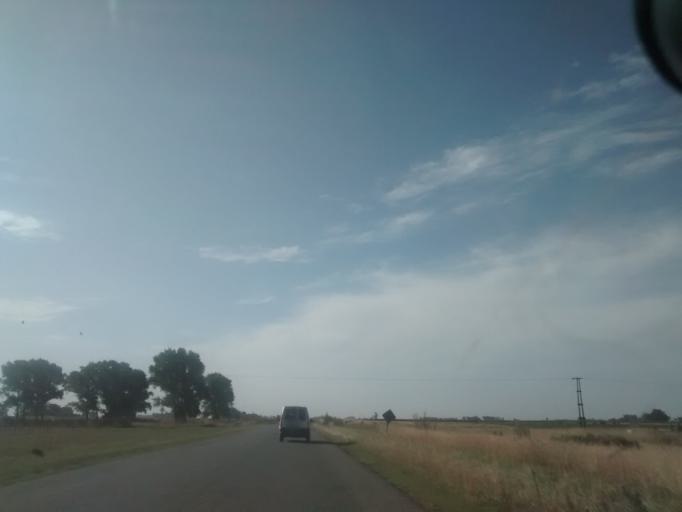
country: AR
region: Buenos Aires
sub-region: Partido de Ayacucho
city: Ayacucho
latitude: -37.1565
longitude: -58.5453
